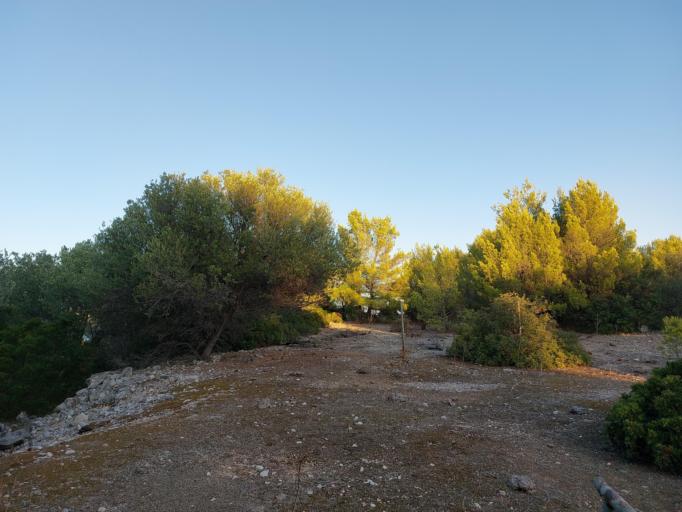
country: HR
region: Dubrovacko-Neretvanska
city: Smokvica
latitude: 42.7318
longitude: 16.8405
